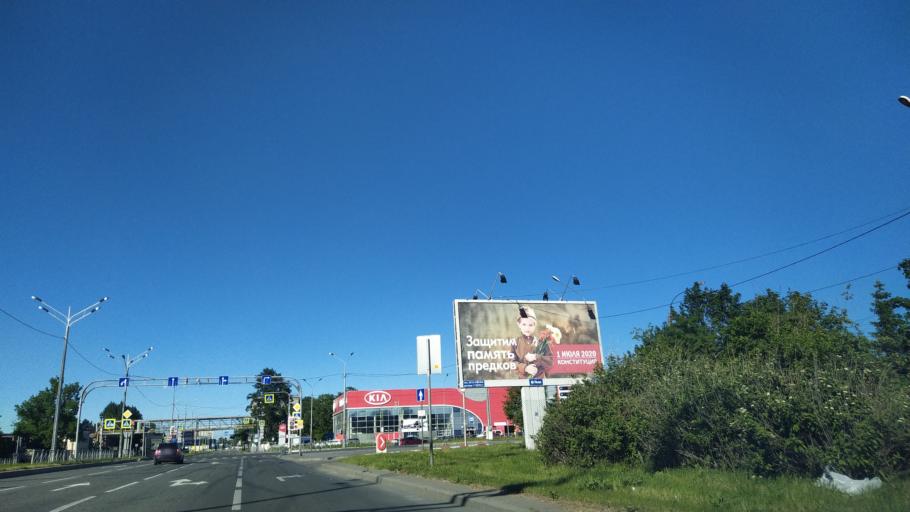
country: RU
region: St.-Petersburg
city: Kupchino
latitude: 59.8888
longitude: 30.3789
